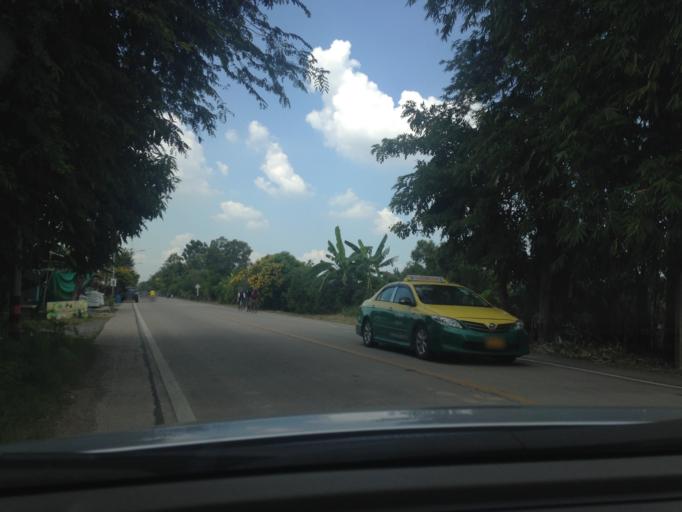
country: TH
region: Pathum Thani
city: Khlong Luang
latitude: 14.0419
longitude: 100.5918
